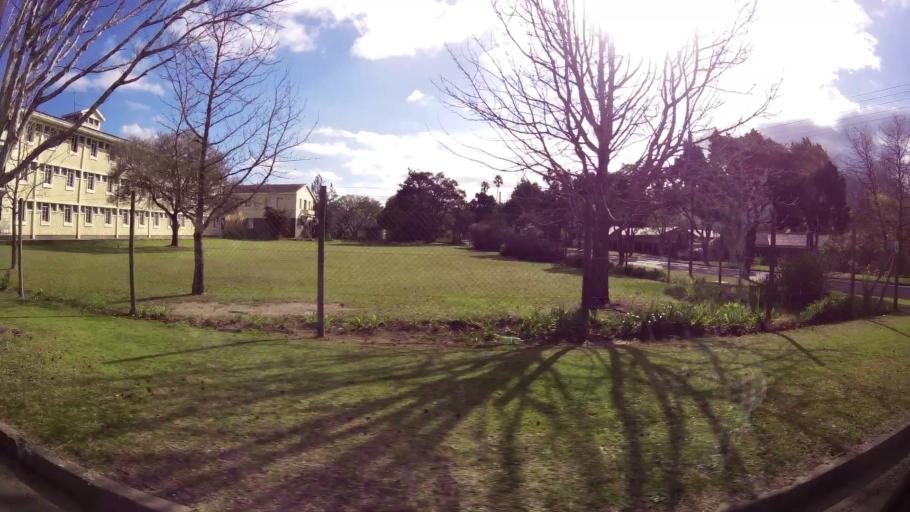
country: ZA
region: Western Cape
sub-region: Eden District Municipality
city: George
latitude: -33.9588
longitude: 22.4823
